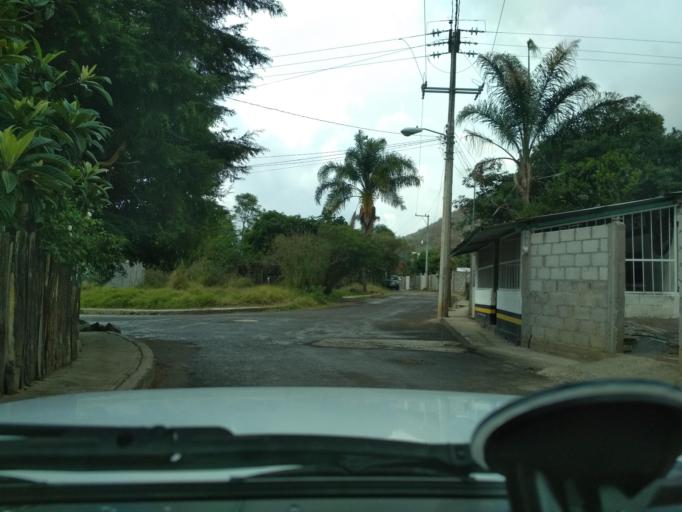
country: MX
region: Veracruz
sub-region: Nogales
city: Taza de Agua Ojo Zarco
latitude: 18.7786
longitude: -97.2030
